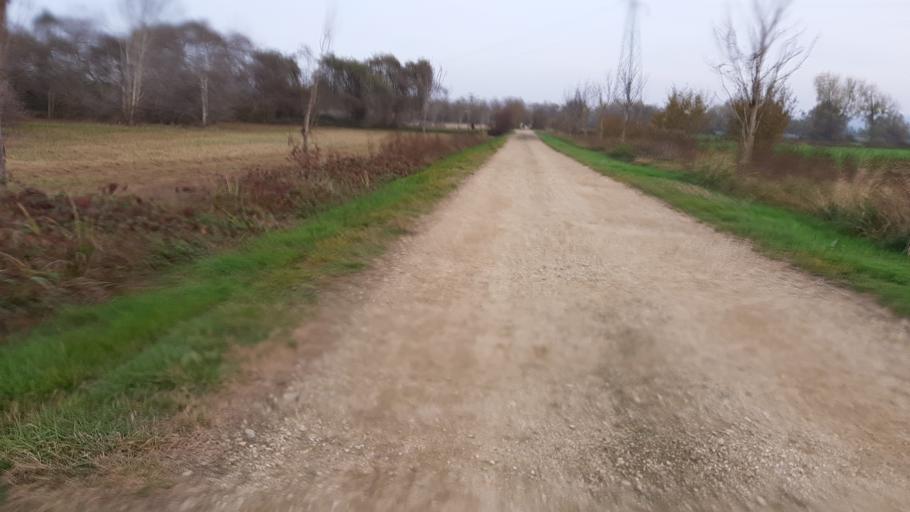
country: IT
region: Piedmont
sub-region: Provincia di Torino
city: Leini
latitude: 45.1402
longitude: 7.7172
